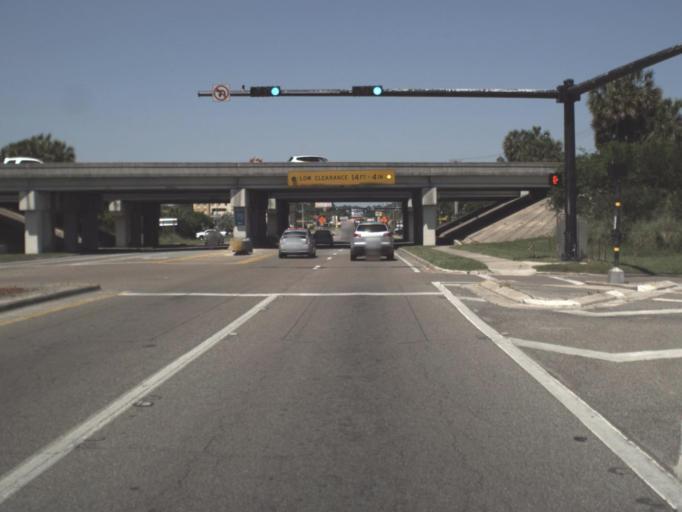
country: US
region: Florida
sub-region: Columbia County
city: Lake City
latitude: 30.1801
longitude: -82.6877
